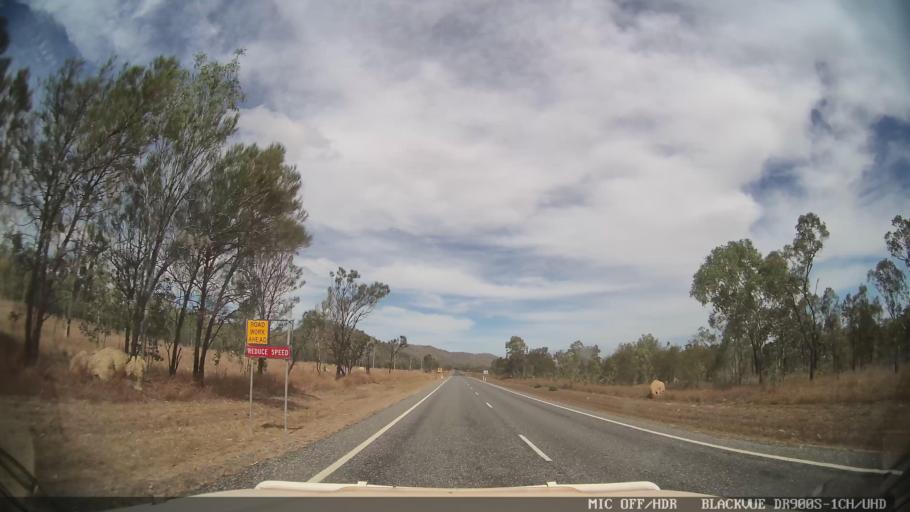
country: AU
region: Queensland
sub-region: Tablelands
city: Mareeba
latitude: -16.7896
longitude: 145.3541
